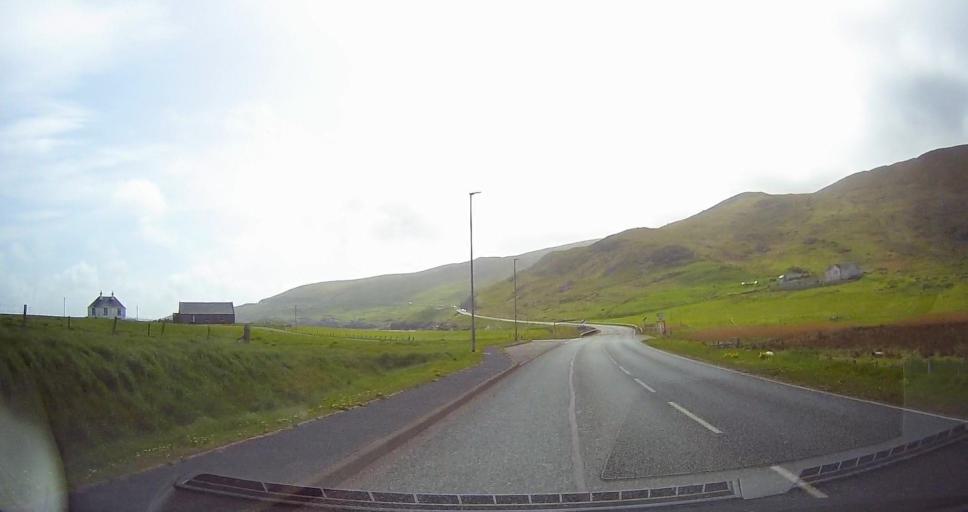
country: GB
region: Scotland
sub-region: Shetland Islands
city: Sandwick
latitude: 60.0366
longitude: -1.2304
